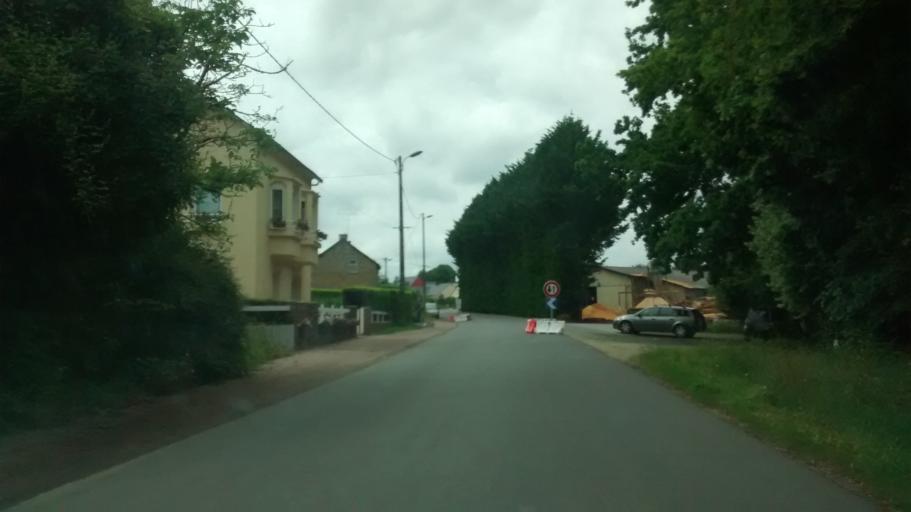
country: FR
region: Brittany
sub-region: Departement du Morbihan
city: Carentoir
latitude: 47.8175
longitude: -2.1402
